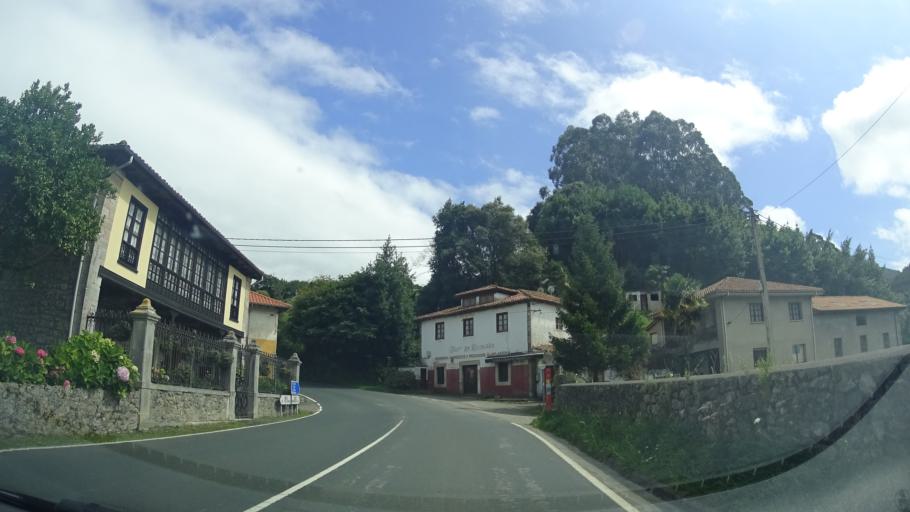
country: ES
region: Asturias
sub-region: Province of Asturias
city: Ribadesella
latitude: 43.4645
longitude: -5.1275
